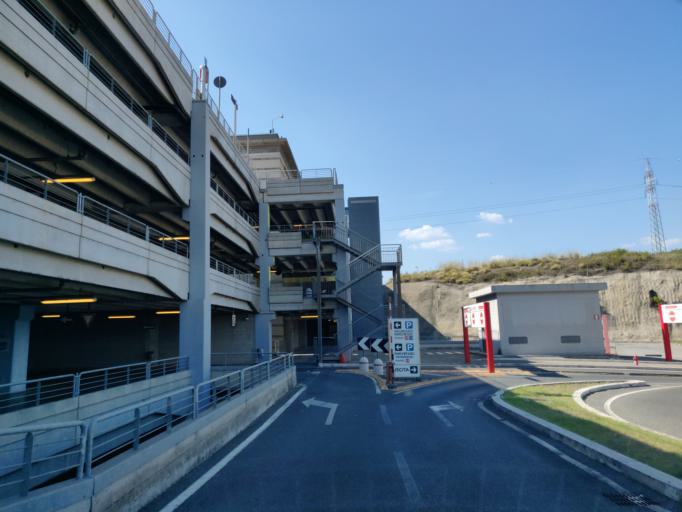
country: IT
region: Latium
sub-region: Citta metropolitana di Roma Capitale
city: Setteville
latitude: 41.9154
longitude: 12.6628
